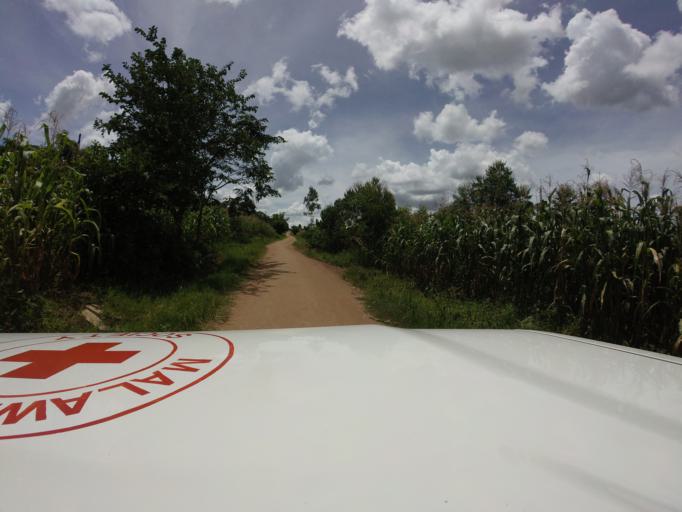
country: MW
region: Southern Region
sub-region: Thyolo District
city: Thyolo
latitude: -15.9551
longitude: 35.1655
